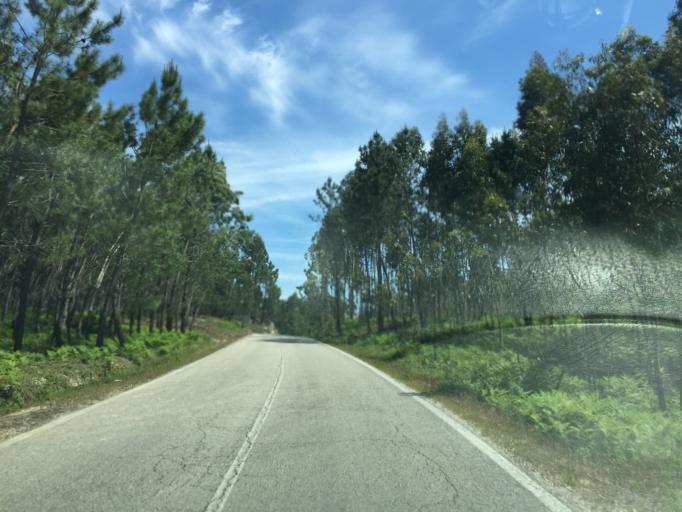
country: PT
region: Coimbra
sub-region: Soure
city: Soure
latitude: 40.0546
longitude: -8.6782
